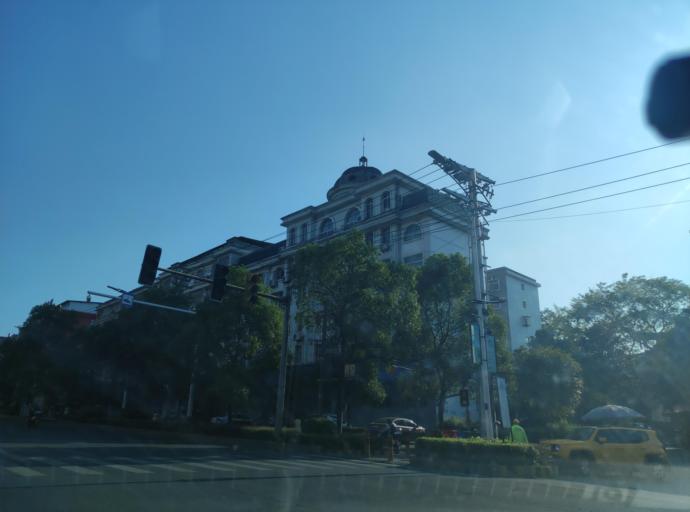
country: CN
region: Jiangxi Sheng
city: Pingxiang
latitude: 27.6331
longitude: 113.8691
